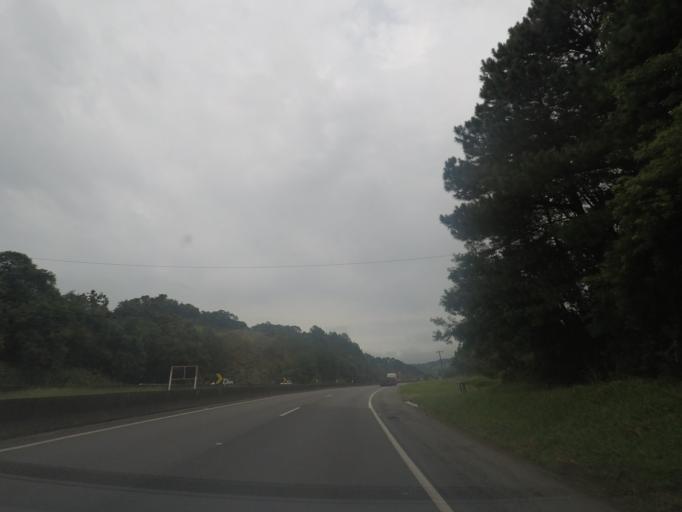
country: BR
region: Parana
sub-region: Campina Grande Do Sul
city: Campina Grande do Sul
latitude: -25.2062
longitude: -48.8955
